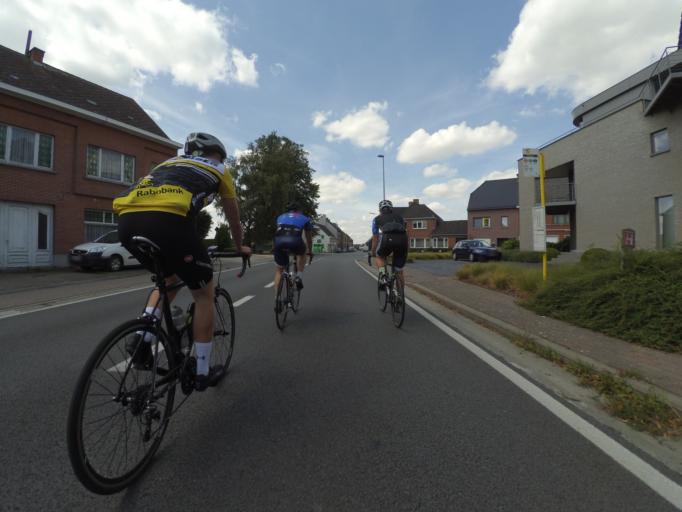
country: BE
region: Flanders
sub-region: Provincie Oost-Vlaanderen
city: Zottegem
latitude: 50.8671
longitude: 3.8002
